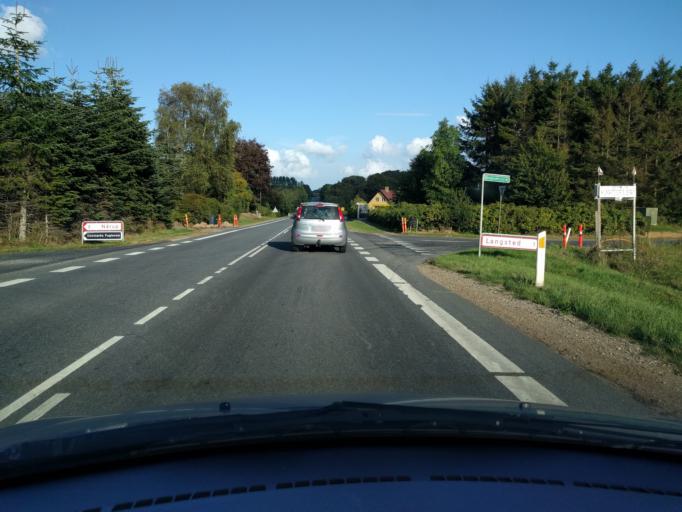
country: DK
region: South Denmark
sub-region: Assens Kommune
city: Tommerup
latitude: 55.2851
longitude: 10.1687
